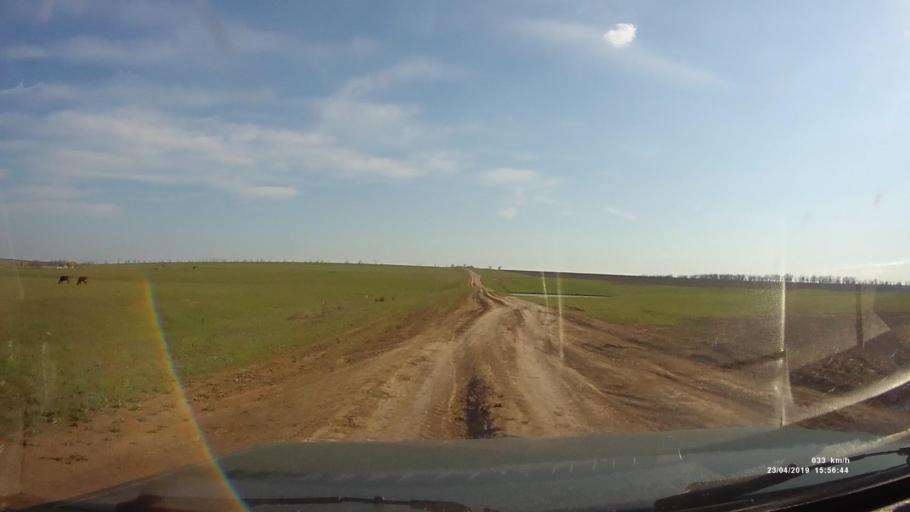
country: RU
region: Rostov
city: Remontnoye
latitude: 46.5355
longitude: 43.1108
